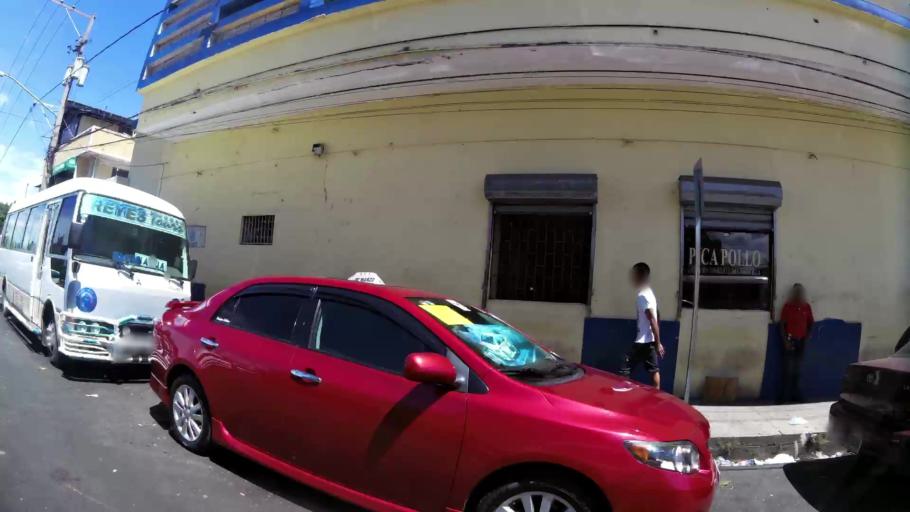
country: DO
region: Santiago
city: Santiago de los Caballeros
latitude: 19.4548
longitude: -70.7052
